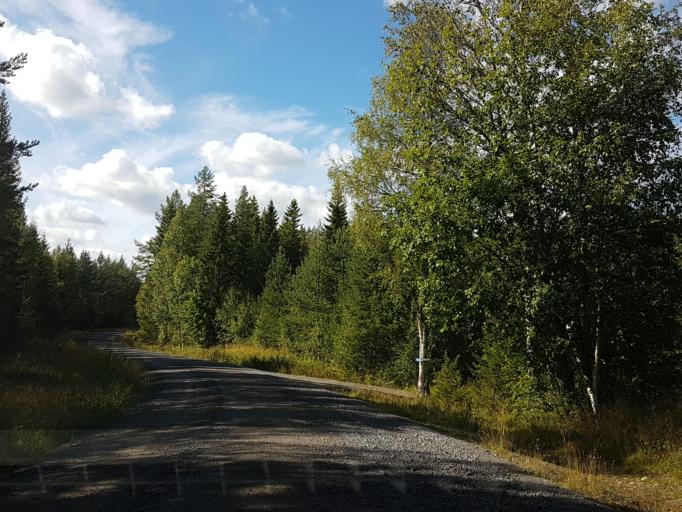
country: SE
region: Vaesterbotten
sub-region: Skelleftea Kommun
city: Burtraesk
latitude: 64.2785
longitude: 20.4785
